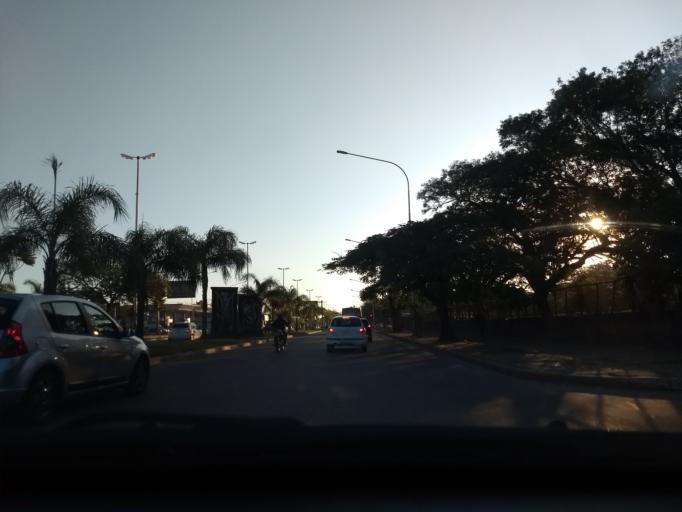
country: AR
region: Corrientes
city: Corrientes
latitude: -27.4779
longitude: -58.8186
